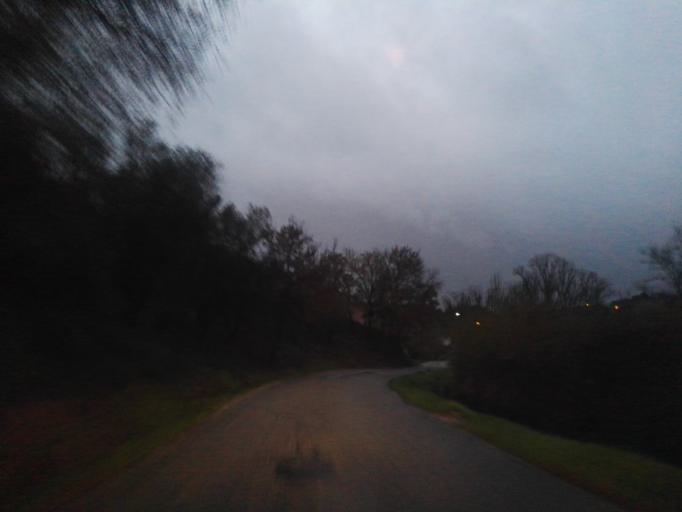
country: PT
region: Santarem
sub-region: Santarem
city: Santarem
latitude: 39.2812
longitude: -8.7901
